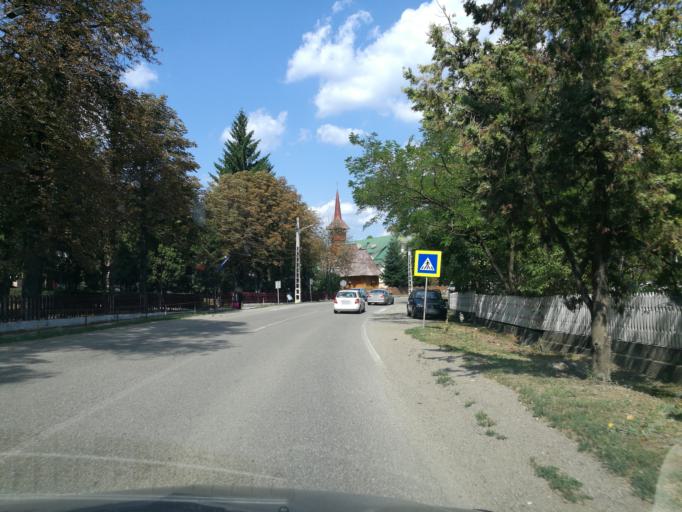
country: RO
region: Neamt
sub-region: Comuna Baltatesti
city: Baltatesti
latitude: 47.1199
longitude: 26.3102
